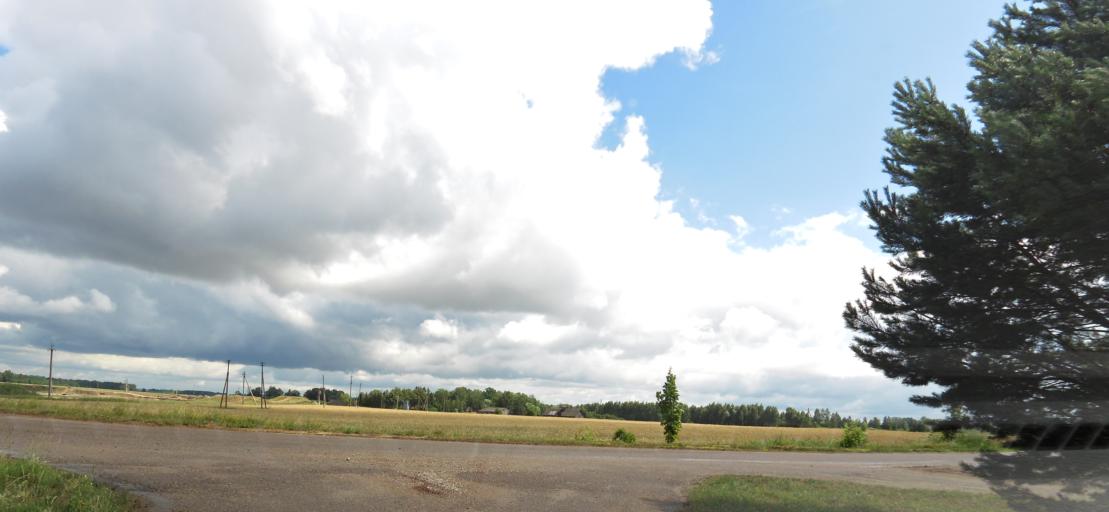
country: LT
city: Vabalninkas
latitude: 55.8864
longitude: 24.7696
